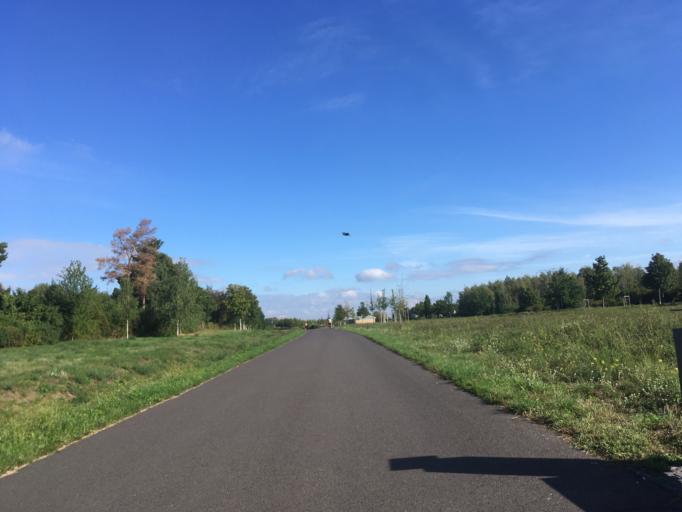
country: DE
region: Berlin
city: Altglienicke
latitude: 52.4149
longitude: 13.5224
